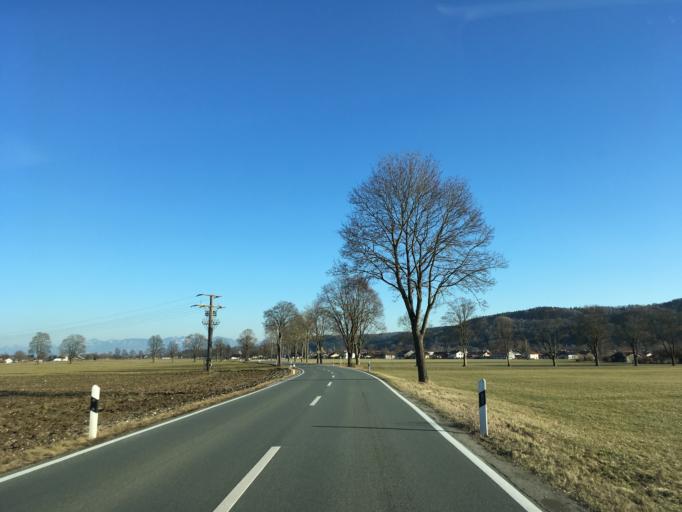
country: DE
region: Bavaria
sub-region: Upper Bavaria
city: Vagen
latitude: 47.8795
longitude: 11.8752
